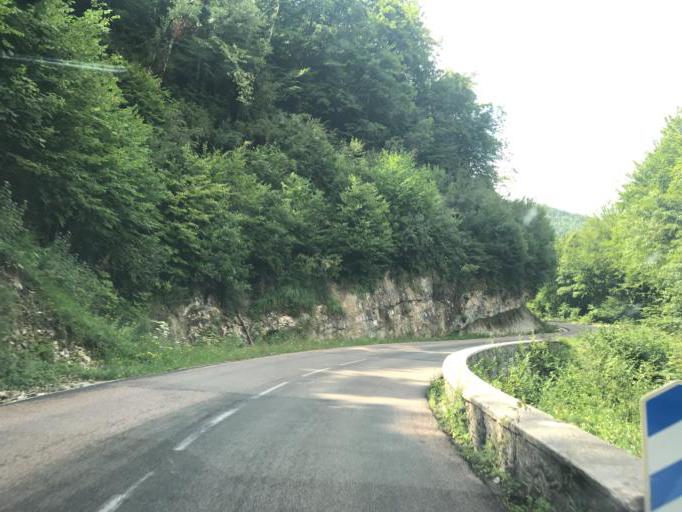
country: FR
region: Franche-Comte
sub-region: Departement du Jura
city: Valfin-les-Saint-Claude
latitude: 46.4164
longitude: 5.8640
